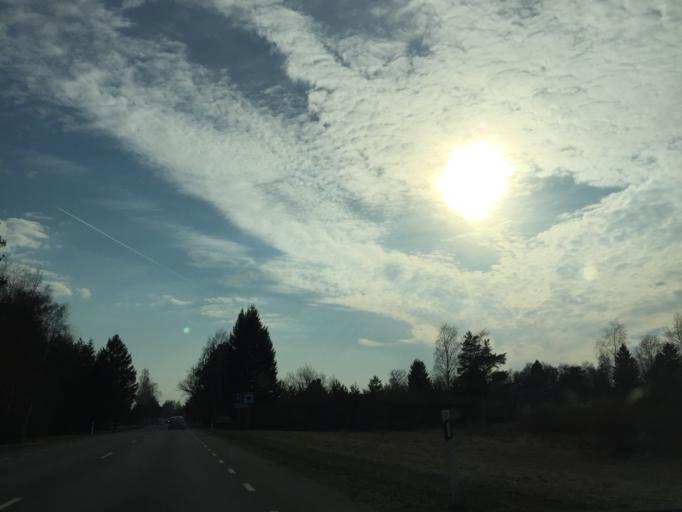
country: EE
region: Jogevamaa
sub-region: Mustvee linn
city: Mustvee
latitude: 58.9001
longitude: 26.9844
